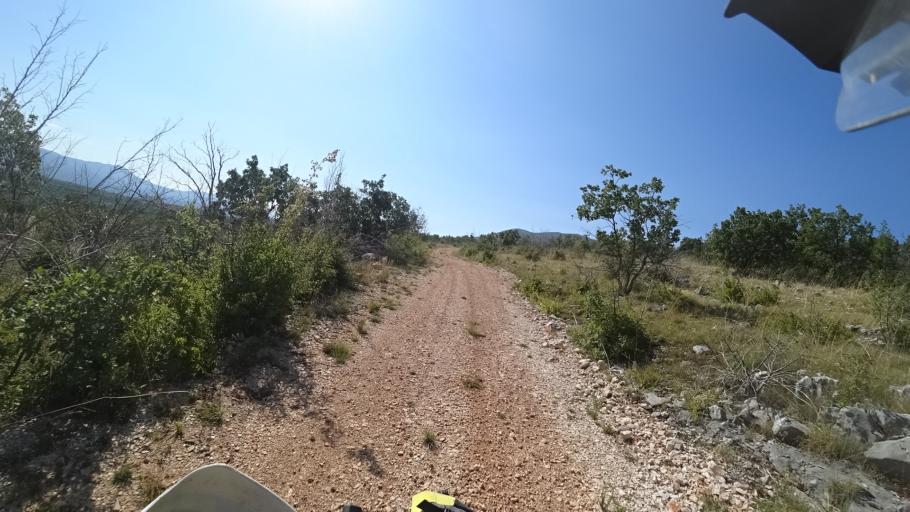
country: HR
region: Sibensko-Kniniska
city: Knin
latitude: 43.9644
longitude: 16.1645
